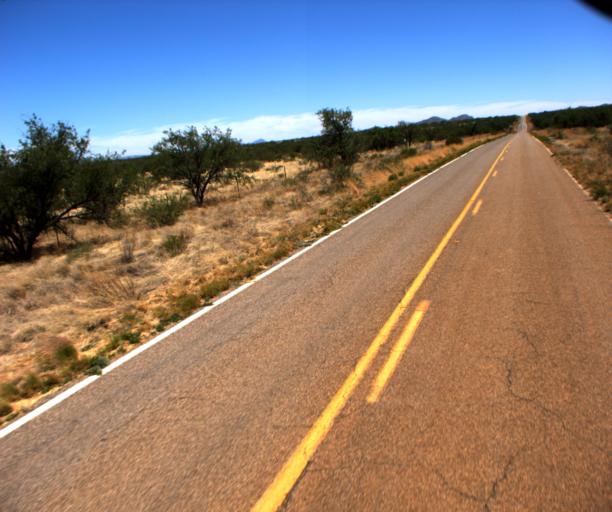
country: US
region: Arizona
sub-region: Santa Cruz County
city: Tubac
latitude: 31.5407
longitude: -111.5405
